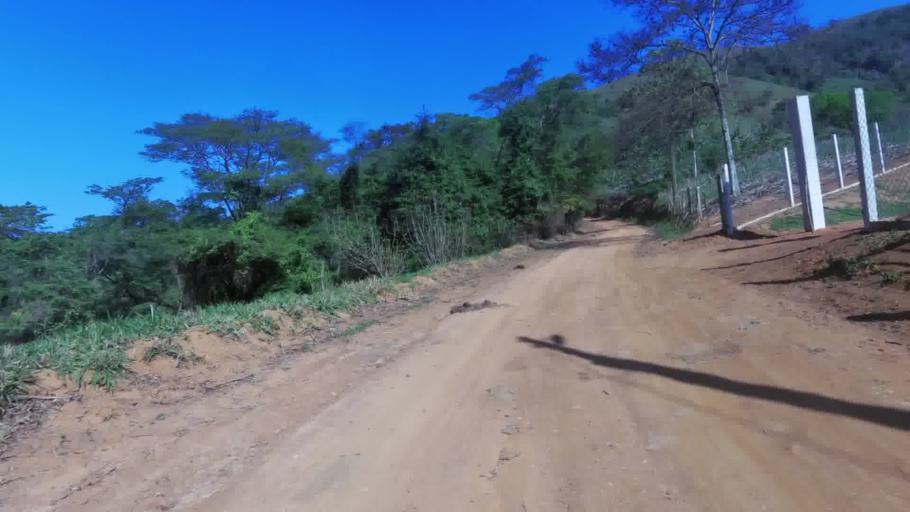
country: BR
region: Espirito Santo
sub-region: Alfredo Chaves
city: Alfredo Chaves
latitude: -20.6824
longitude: -40.7742
